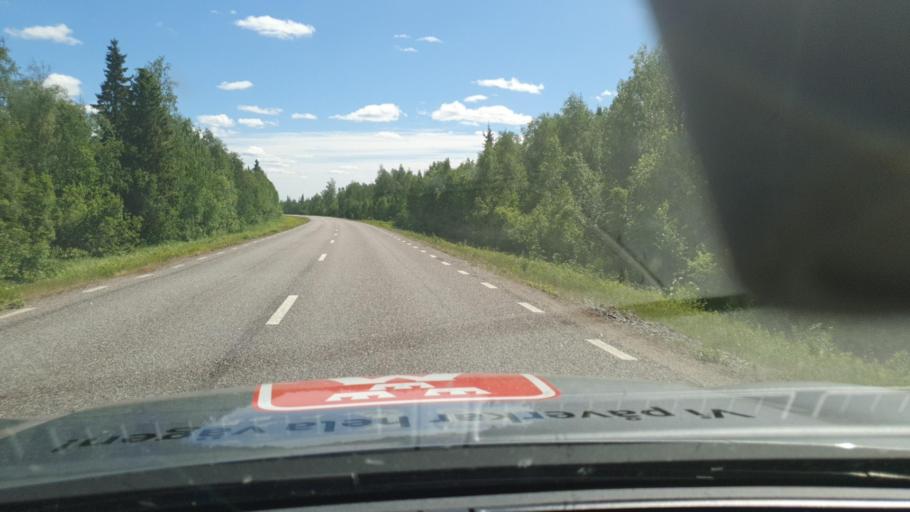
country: SE
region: Norrbotten
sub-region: Pajala Kommun
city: Pajala
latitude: 67.1189
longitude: 23.6073
